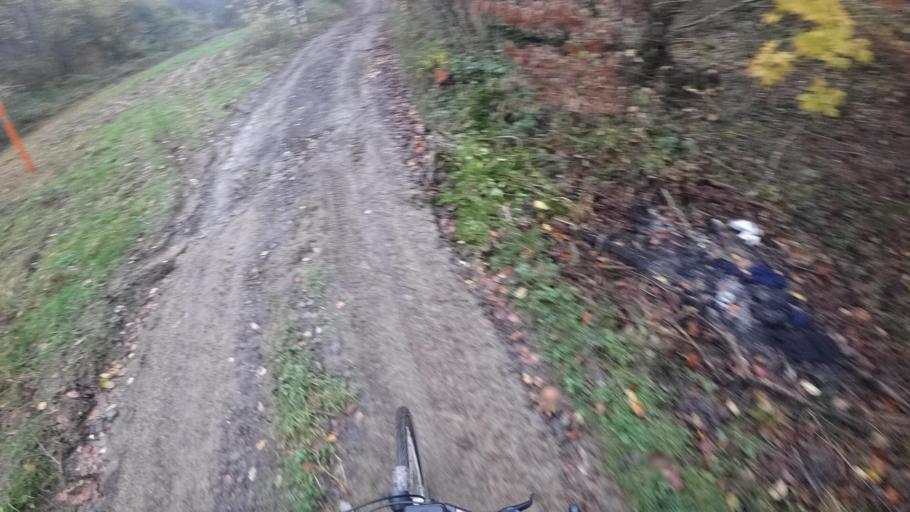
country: DE
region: Rheinland-Pfalz
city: Rech
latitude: 50.5184
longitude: 7.0464
